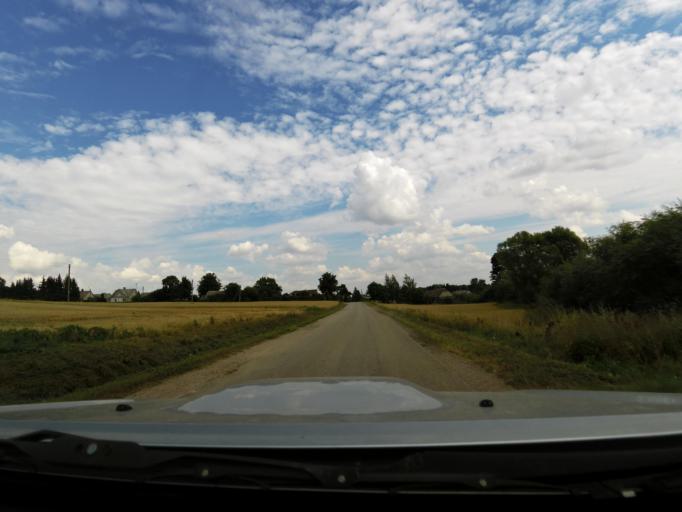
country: LT
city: Gelgaudiskis
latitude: 55.0989
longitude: 22.9720
